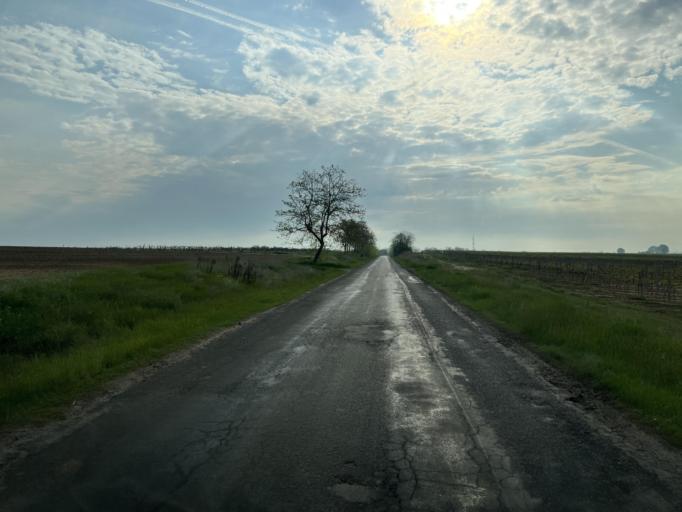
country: HU
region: Pest
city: Cegledbercel
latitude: 47.2172
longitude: 19.6935
